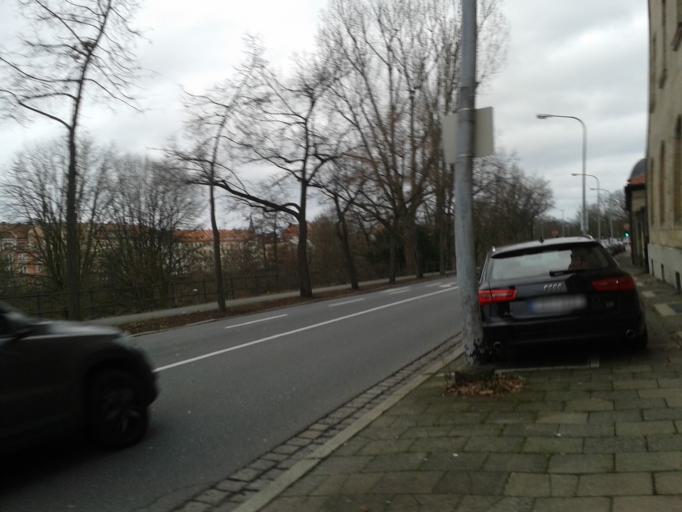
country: DE
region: Bavaria
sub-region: Upper Franconia
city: Bamberg
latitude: 49.8918
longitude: 10.8981
